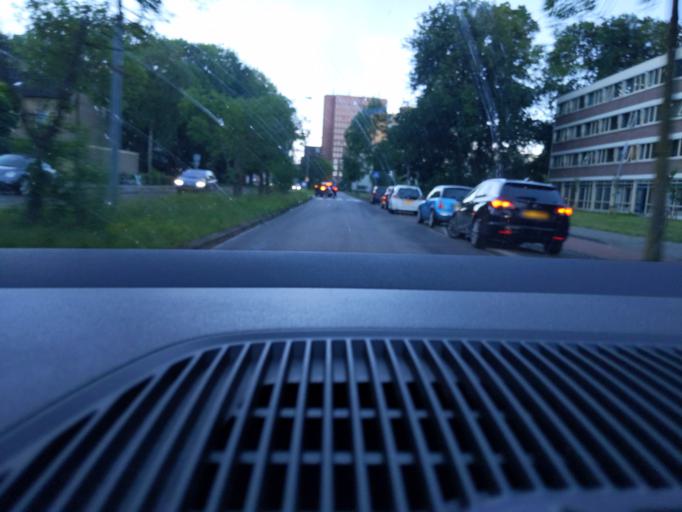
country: NL
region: Groningen
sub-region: Gemeente Groningen
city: Korrewegwijk
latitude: 53.2333
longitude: 6.5399
